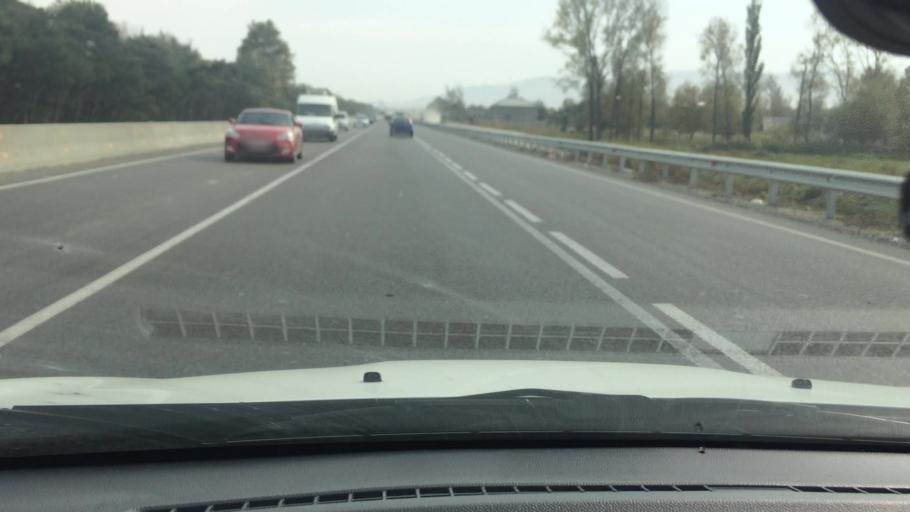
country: GE
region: Kvemo Kartli
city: Rust'avi
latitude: 41.6260
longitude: 44.9238
